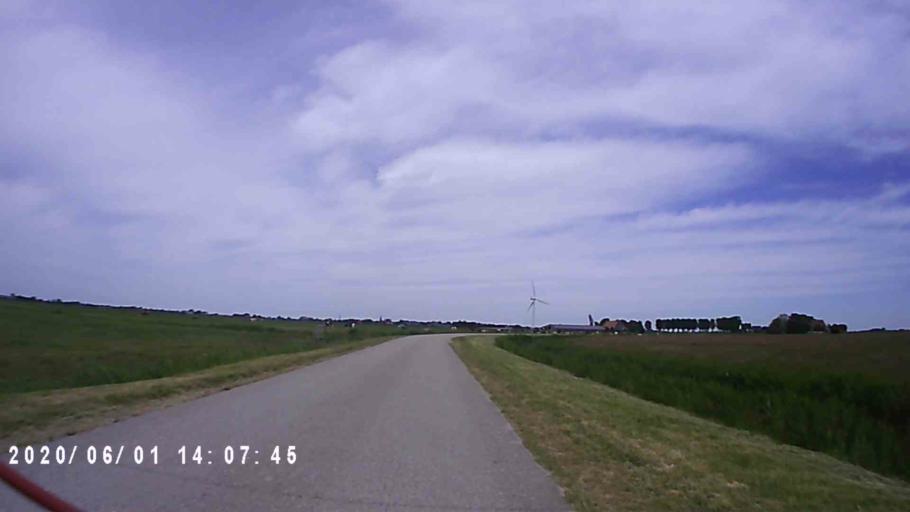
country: NL
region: Friesland
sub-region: Gemeente Littenseradiel
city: Winsum
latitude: 53.1186
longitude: 5.6410
